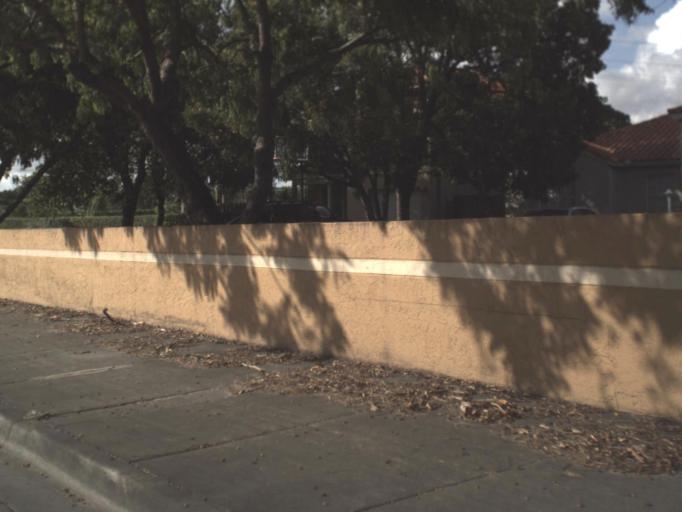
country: US
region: Florida
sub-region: Miami-Dade County
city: Three Lakes
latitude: 25.6267
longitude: -80.4044
